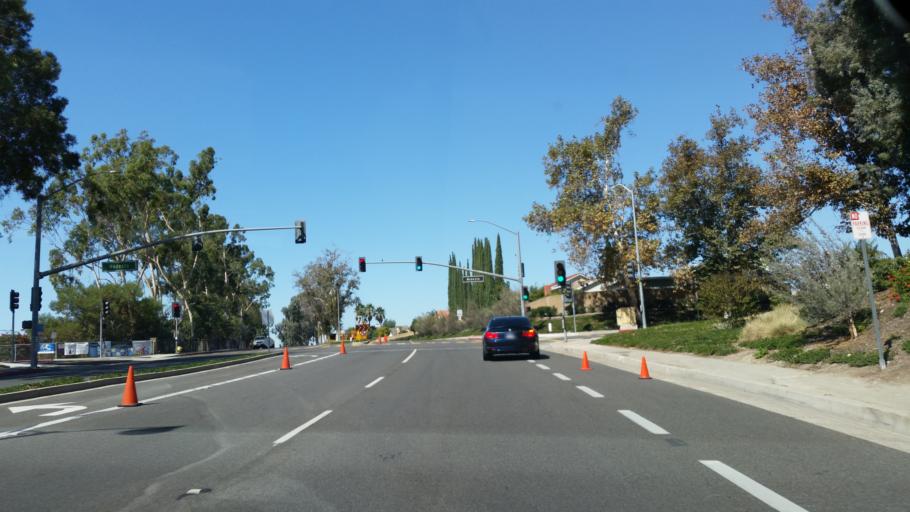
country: US
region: California
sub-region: Orange County
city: Lake Forest
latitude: 33.6298
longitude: -117.6668
